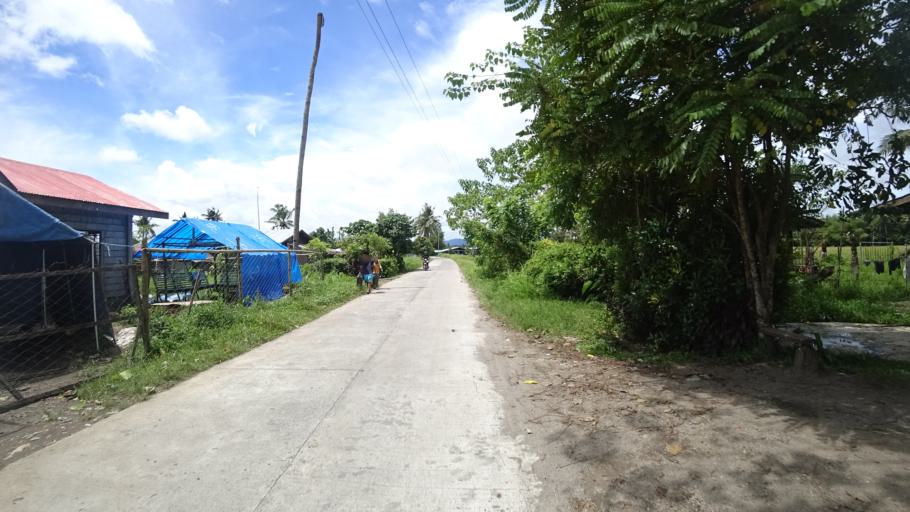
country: PH
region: Eastern Visayas
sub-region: Province of Leyte
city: Alangalang
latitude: 11.2175
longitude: 124.8460
